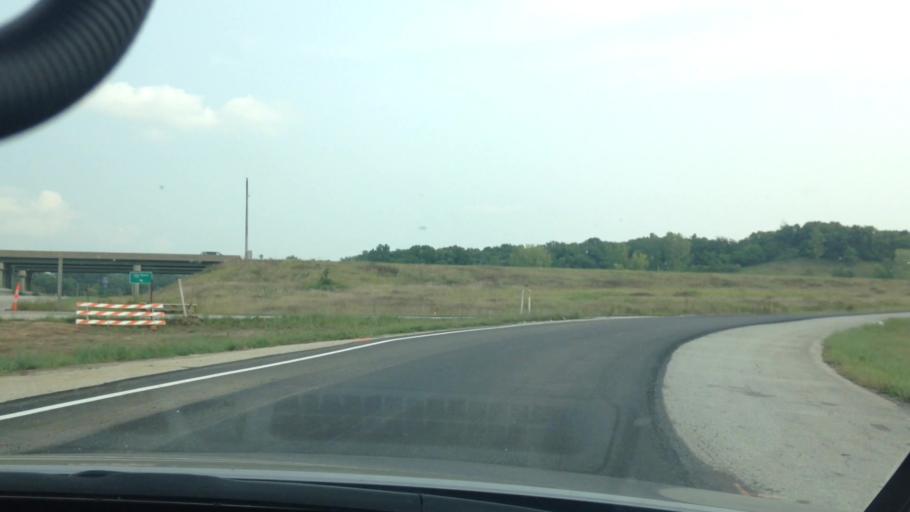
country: US
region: Missouri
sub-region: Platte County
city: Weatherby Lake
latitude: 39.1806
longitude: -94.8007
